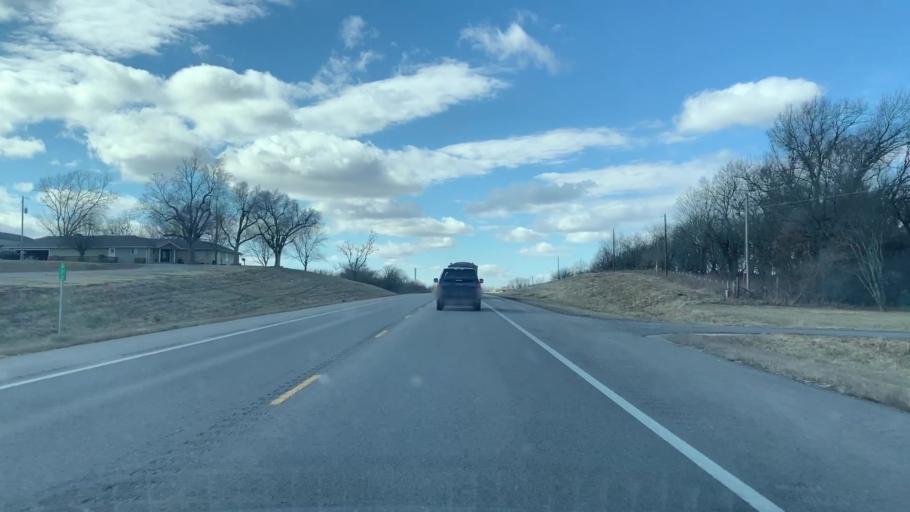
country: US
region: Kansas
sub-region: Cherokee County
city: Columbus
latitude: 37.3400
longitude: -94.8953
